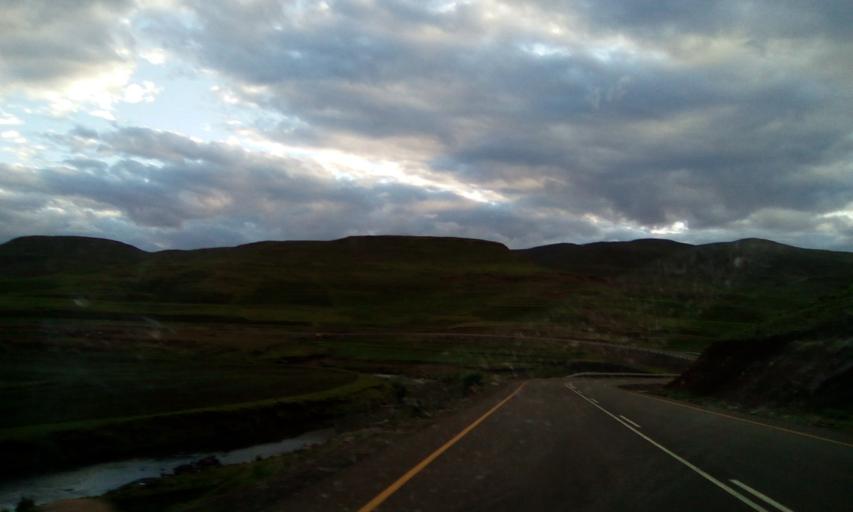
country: LS
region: Maseru
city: Nako
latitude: -29.8042
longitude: 28.0297
